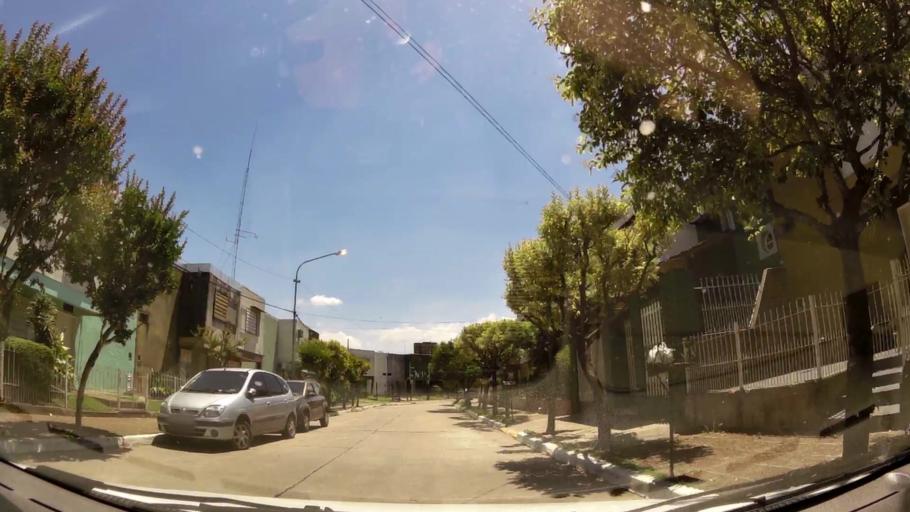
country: AR
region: Buenos Aires
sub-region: Partido de Merlo
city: Merlo
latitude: -34.6527
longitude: -58.7114
